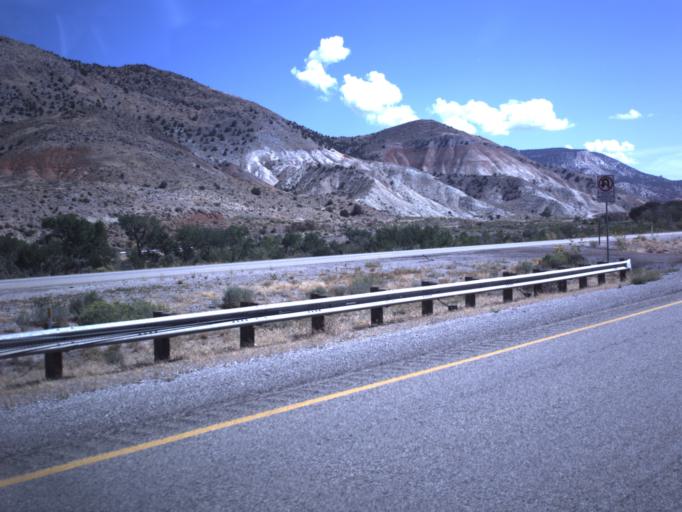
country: US
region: Utah
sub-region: Sevier County
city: Salina
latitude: 38.9317
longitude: -111.8431
